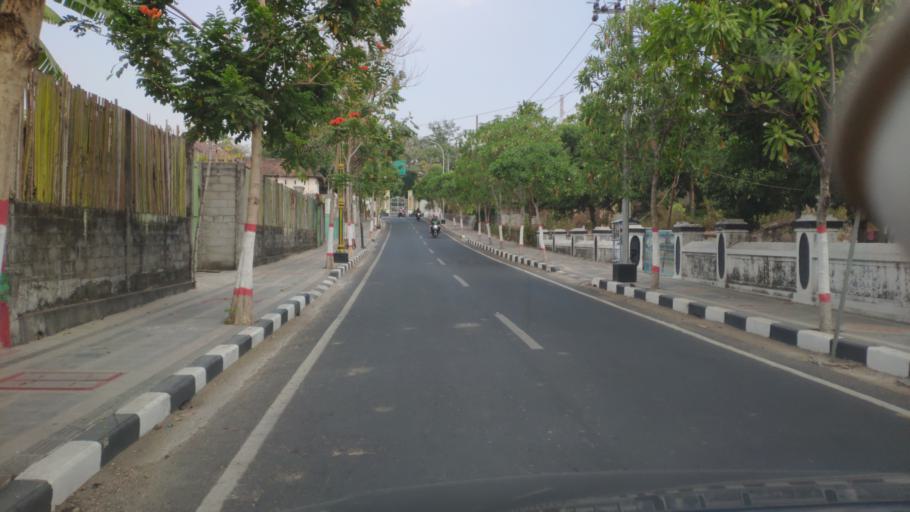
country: ID
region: Central Java
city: Kauman
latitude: -6.9674
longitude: 111.4118
